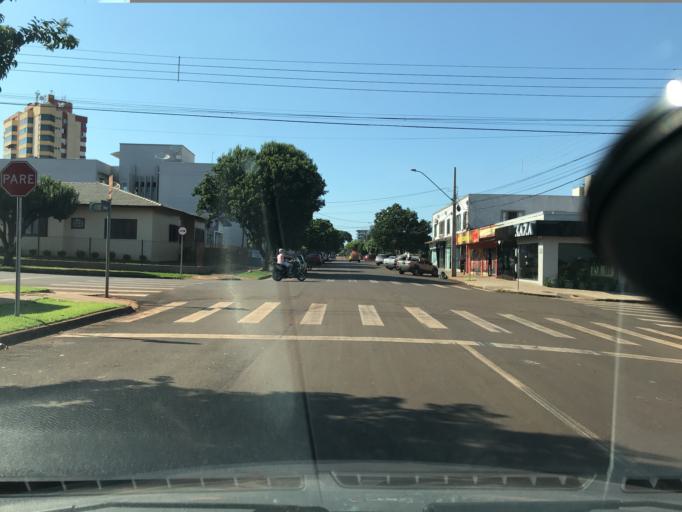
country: BR
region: Parana
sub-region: Palotina
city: Palotina
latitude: -24.2811
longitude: -53.8420
